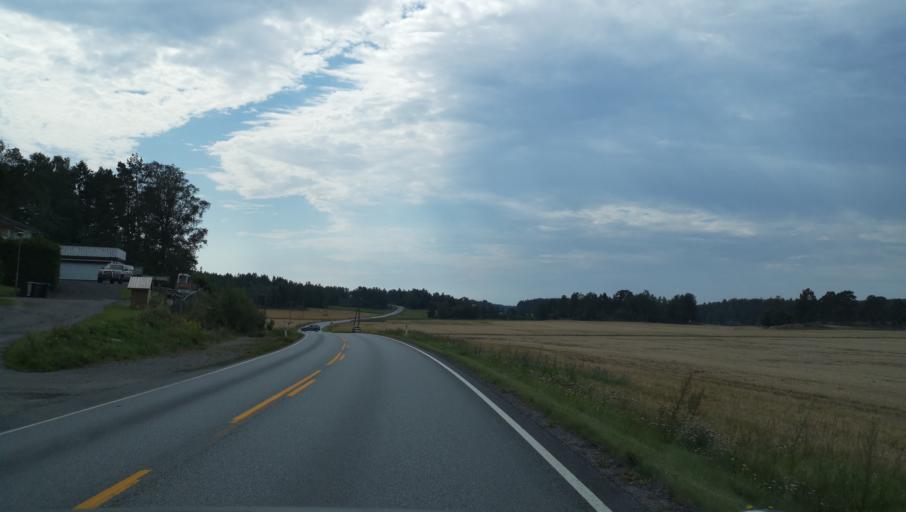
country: NO
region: Ostfold
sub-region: Valer
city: Kirkebygda
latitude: 59.4786
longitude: 10.7914
